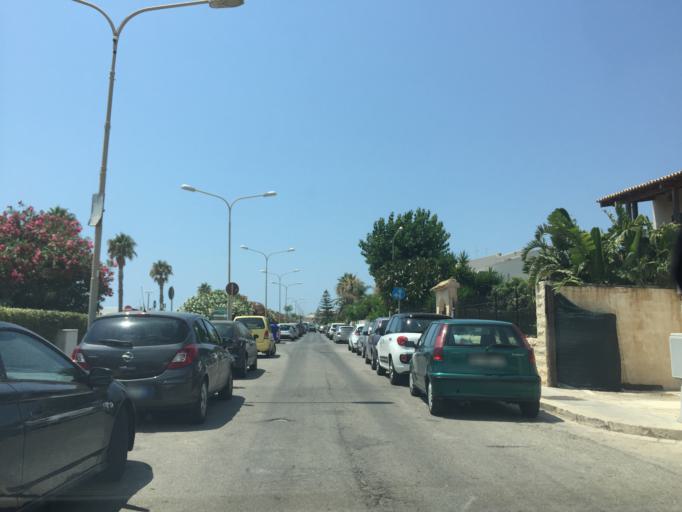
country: IT
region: Sicily
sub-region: Ragusa
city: Marina di Ragusa
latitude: 36.7812
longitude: 14.5668
